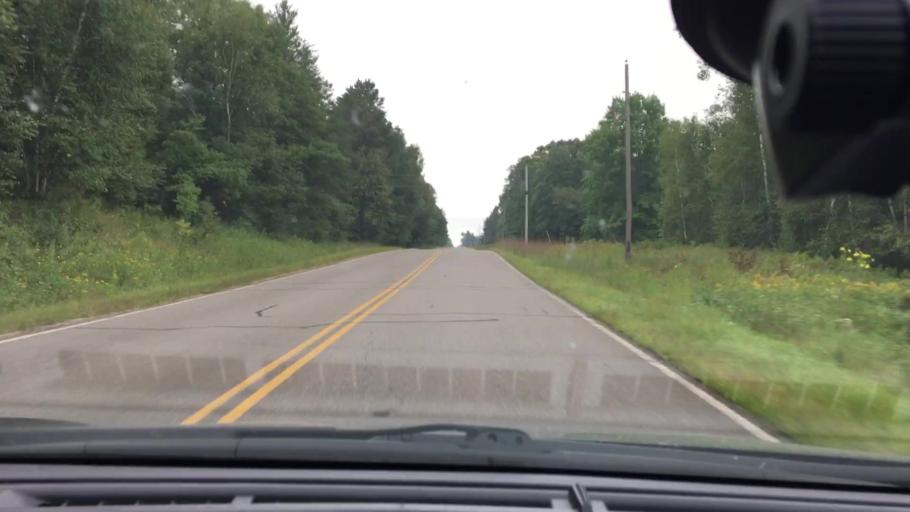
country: US
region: Minnesota
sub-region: Crow Wing County
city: Cross Lake
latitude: 46.6521
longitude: -94.0094
